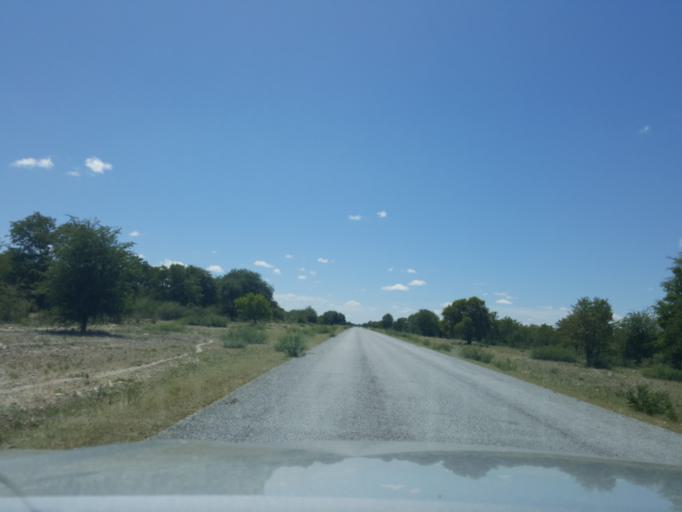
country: BW
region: Central
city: Gweta
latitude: -20.1742
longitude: 25.3776
